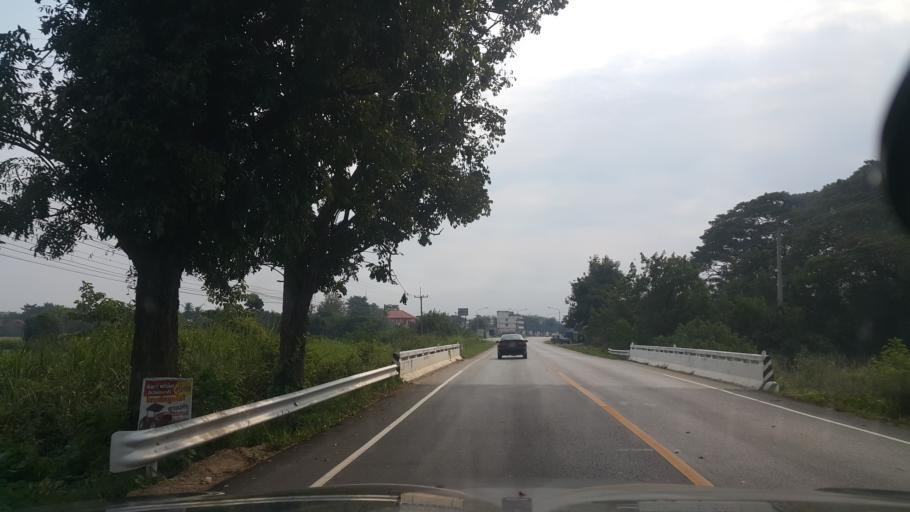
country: TH
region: Sukhothai
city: Si Samrong
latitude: 17.1768
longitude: 99.8484
